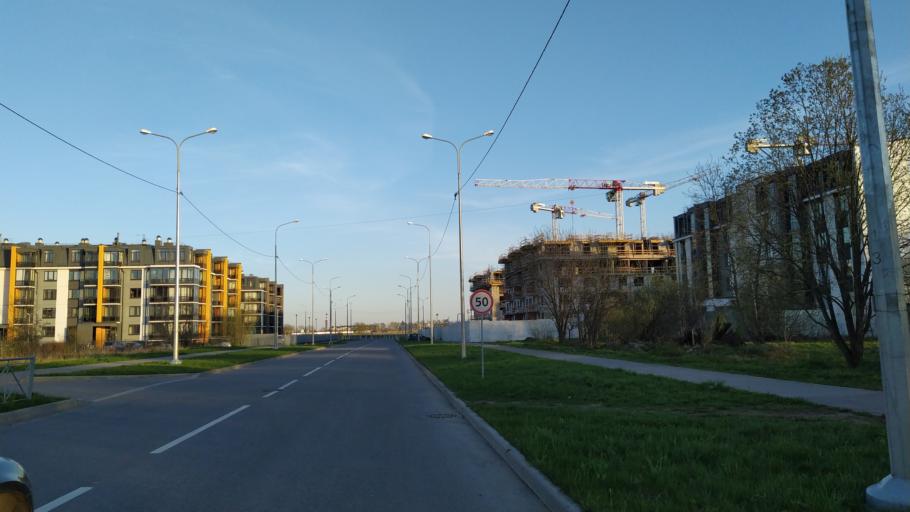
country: RU
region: St.-Petersburg
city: Pushkin
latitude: 59.7010
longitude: 30.4008
